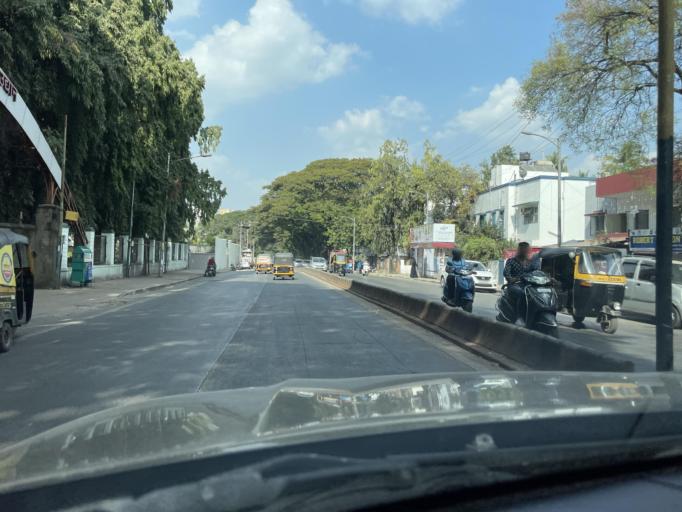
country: IN
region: Maharashtra
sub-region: Pune Division
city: Pune
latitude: 18.4980
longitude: 73.9003
